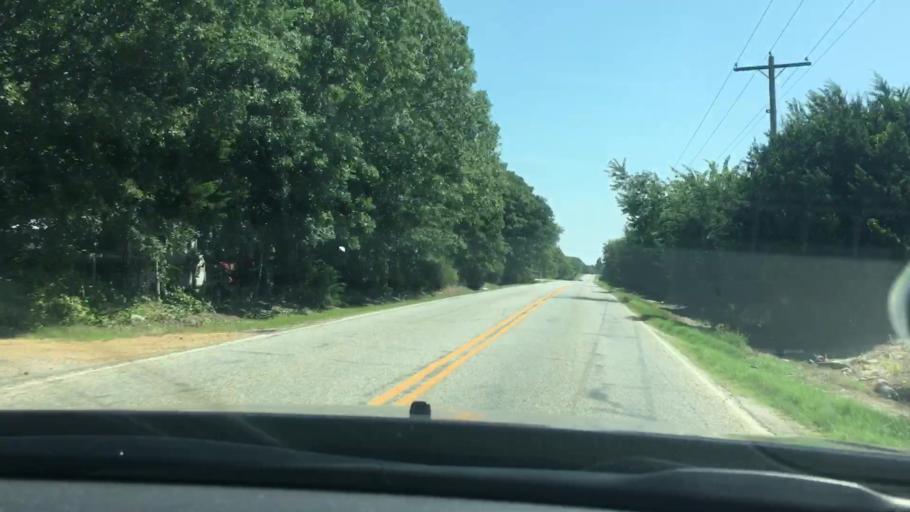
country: US
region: Oklahoma
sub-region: Johnston County
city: Tishomingo
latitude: 34.2377
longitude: -96.5773
